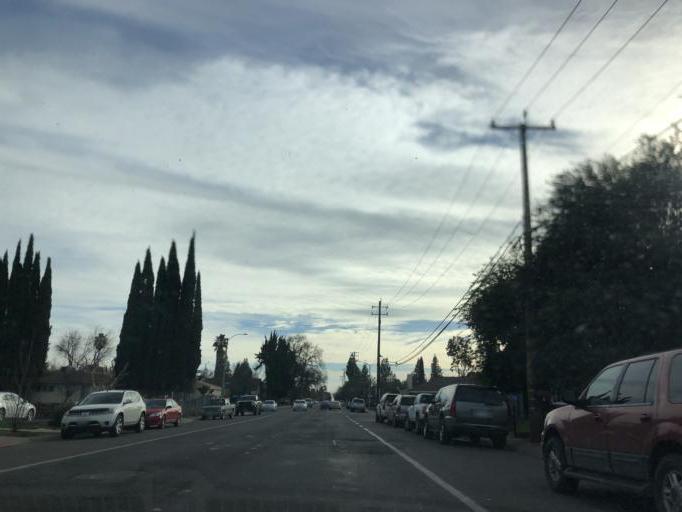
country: US
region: California
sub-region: Yolo County
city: Woodland
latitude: 38.6743
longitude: -121.7561
